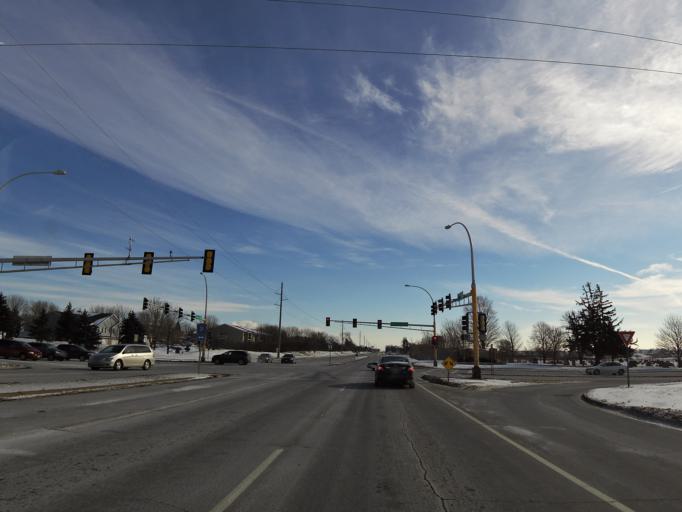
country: US
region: Minnesota
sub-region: Dakota County
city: Apple Valley
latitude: 44.7319
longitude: -93.1777
